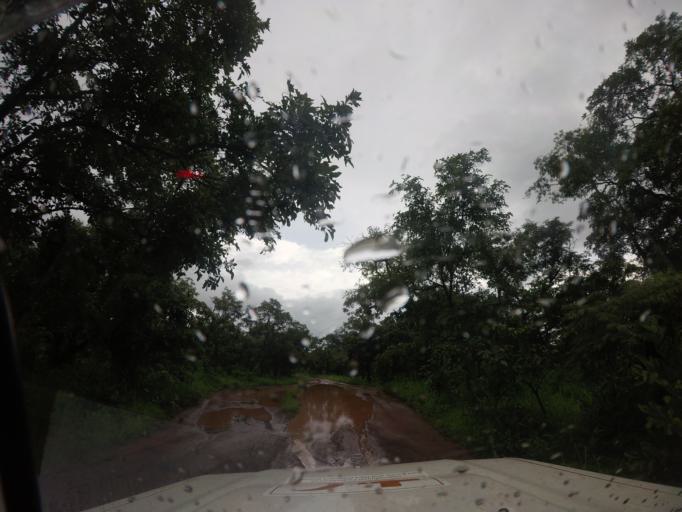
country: SL
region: Northern Province
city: Kamakwie
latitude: 9.7959
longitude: -12.3603
